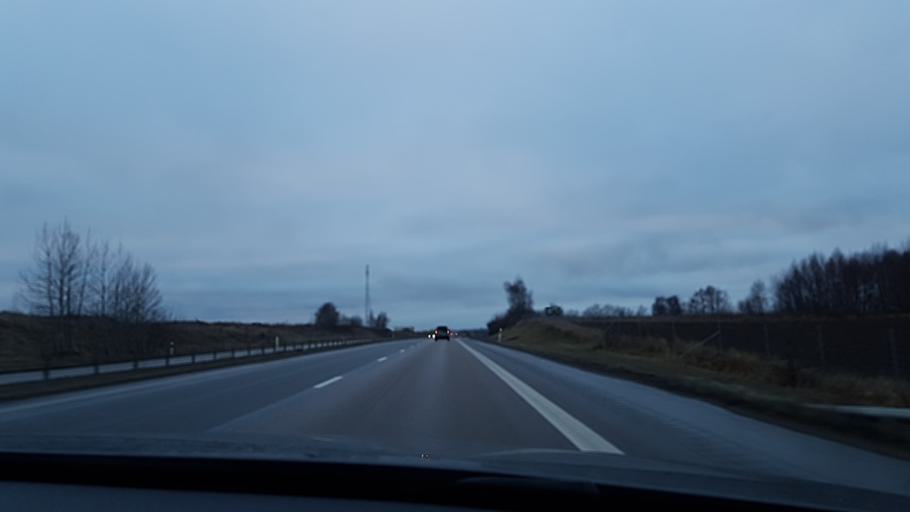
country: SE
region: Skane
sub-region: Astorps Kommun
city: Kvidinge
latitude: 56.1851
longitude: 13.0381
